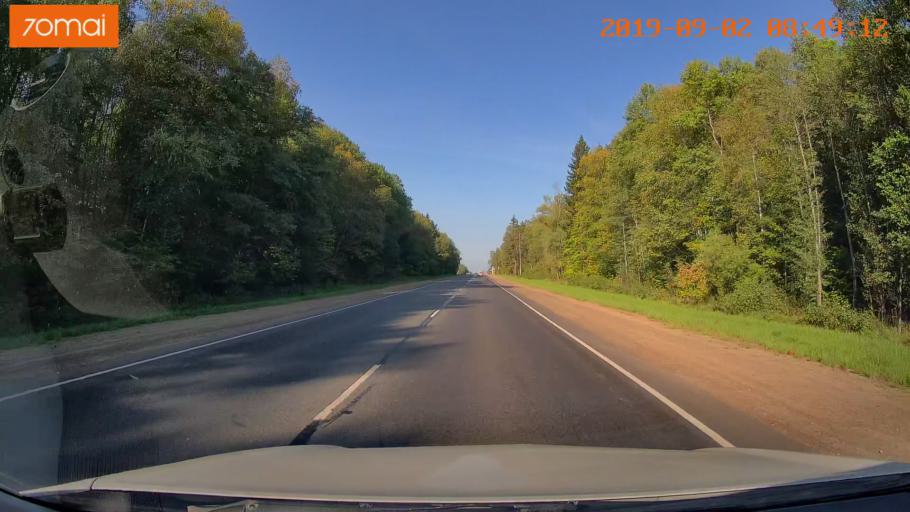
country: RU
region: Kaluga
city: Medyn'
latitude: 54.9663
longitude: 35.9120
